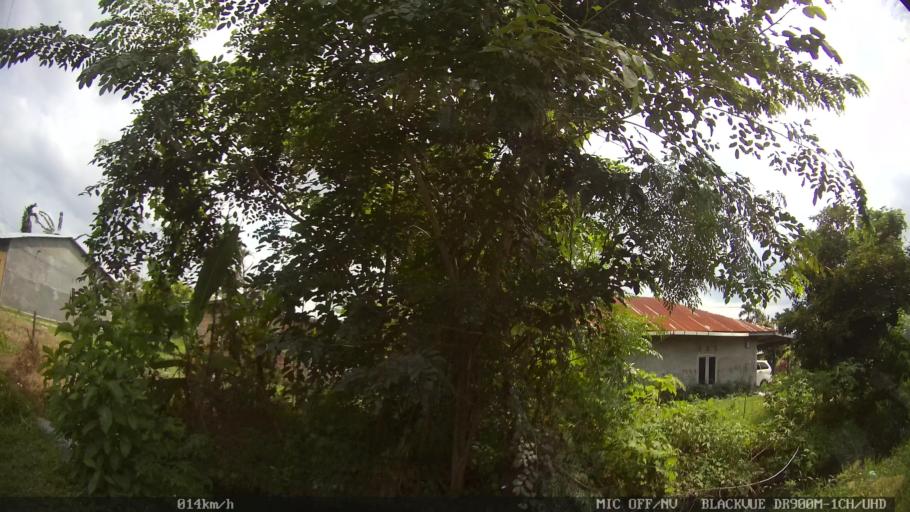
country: ID
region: North Sumatra
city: Sunggal
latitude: 3.6238
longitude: 98.6010
